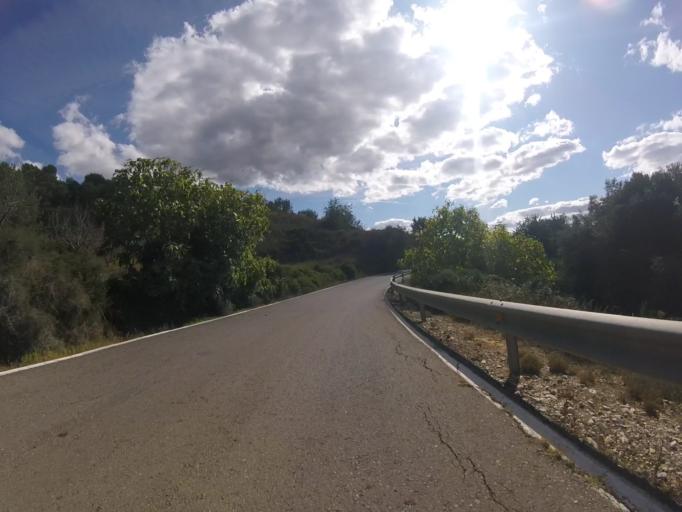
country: ES
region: Valencia
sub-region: Provincia de Castello
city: Cuevas de Vinroma
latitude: 40.3670
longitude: 0.1214
